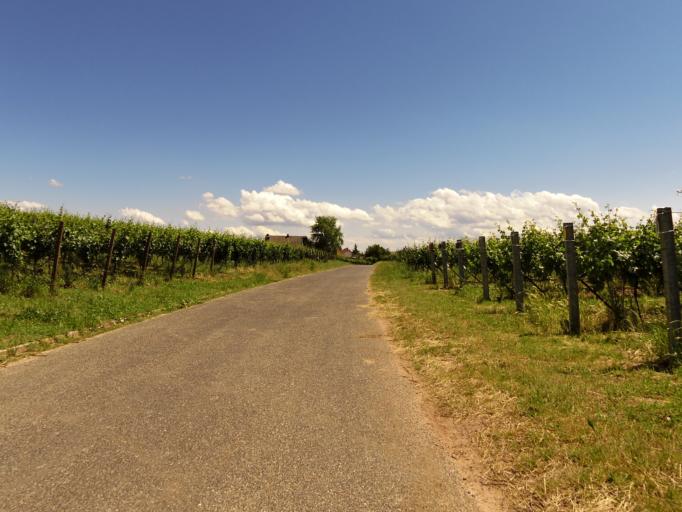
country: DE
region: Rheinland-Pfalz
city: Hainfeld
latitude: 49.2592
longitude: 8.0910
